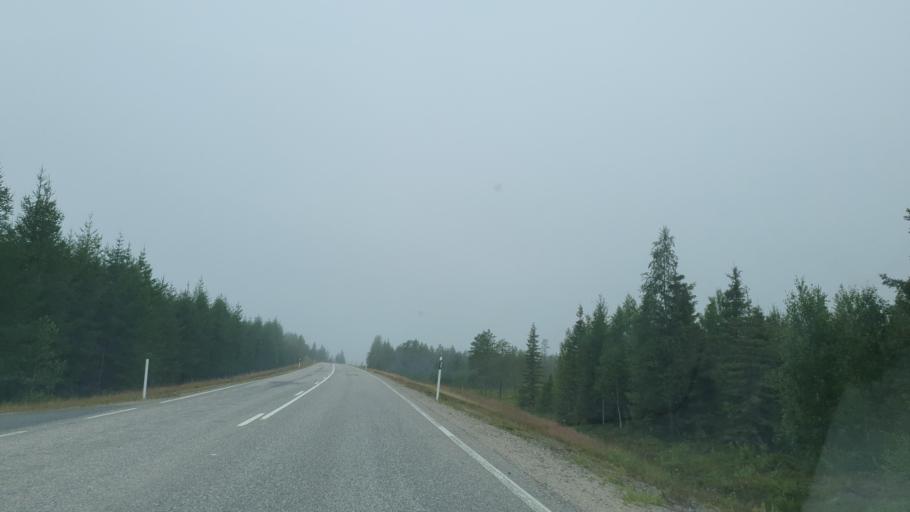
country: FI
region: Lapland
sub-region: Itae-Lappi
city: Salla
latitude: 66.3919
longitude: 28.6505
